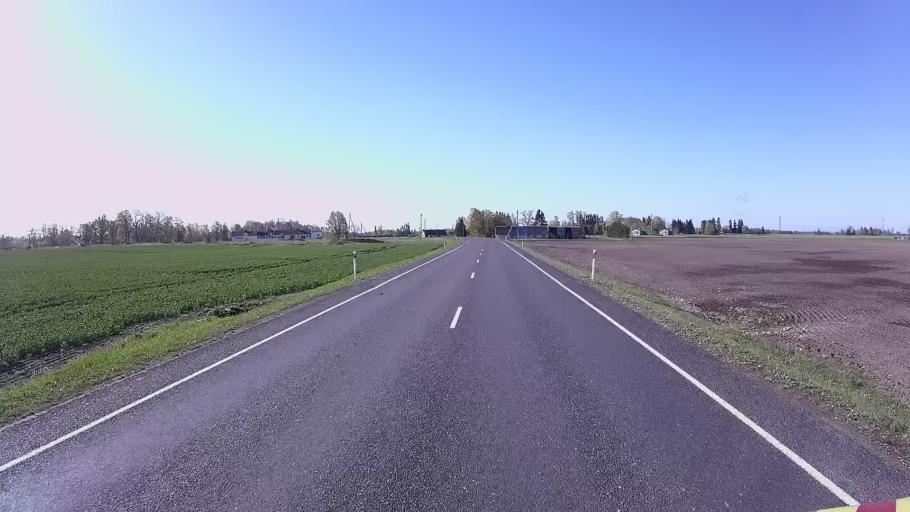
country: EE
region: Viljandimaa
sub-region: Vohma linn
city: Vohma
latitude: 58.6640
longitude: 25.6078
